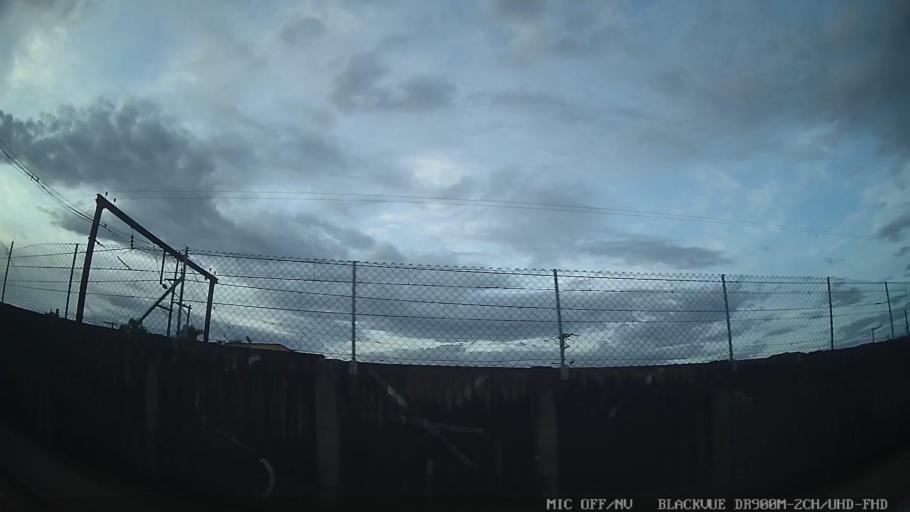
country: BR
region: Sao Paulo
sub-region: Mogi das Cruzes
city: Mogi das Cruzes
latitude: -23.5339
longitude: -46.2176
